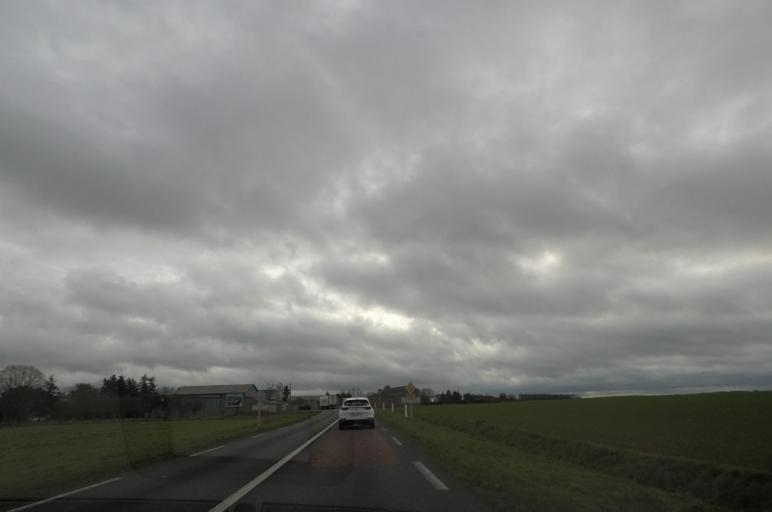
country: FR
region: Centre
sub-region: Departement du Loir-et-Cher
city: Herbault
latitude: 47.6900
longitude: 1.1915
